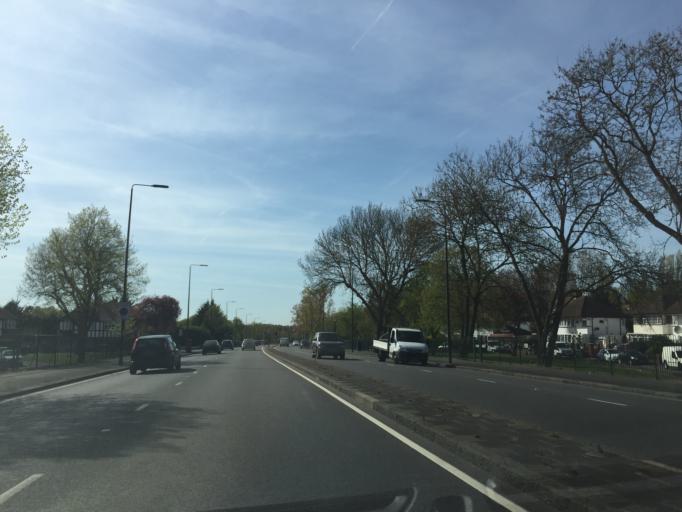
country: GB
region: England
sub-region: Greater London
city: Chislehurst
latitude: 51.4408
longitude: 0.0426
